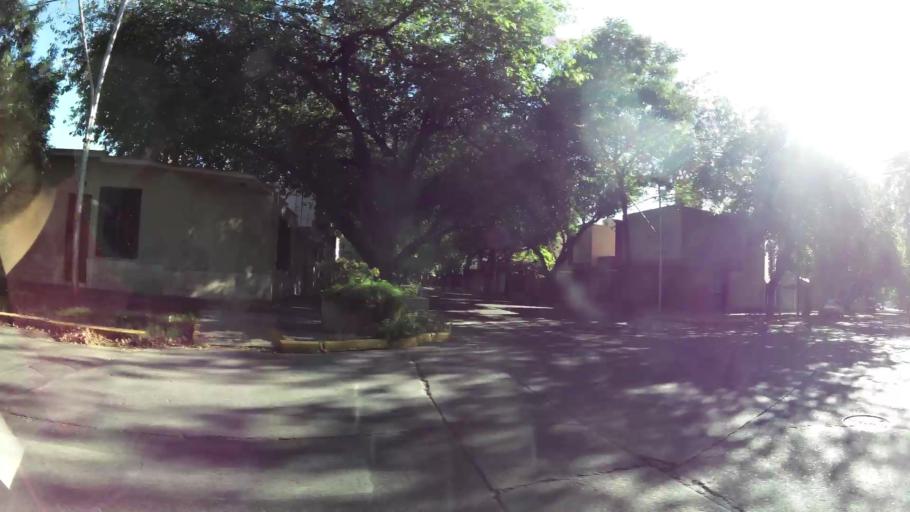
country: AR
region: Mendoza
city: Las Heras
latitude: -32.8660
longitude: -68.8358
